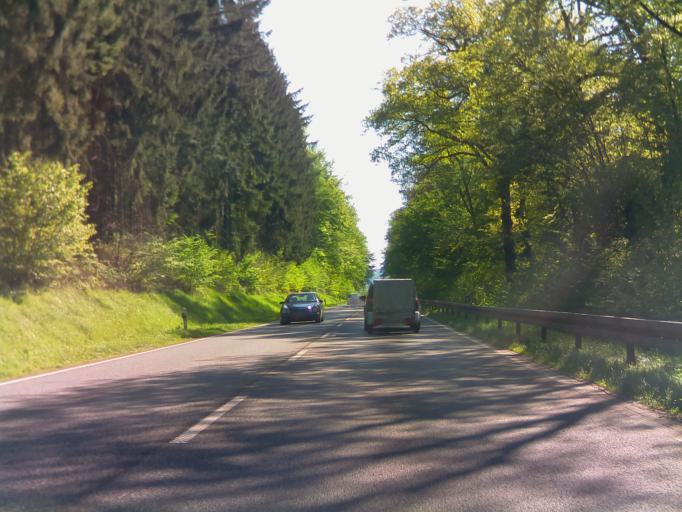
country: DE
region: Hesse
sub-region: Regierungsbezirk Darmstadt
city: Wachtersbach
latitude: 50.2463
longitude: 9.2976
